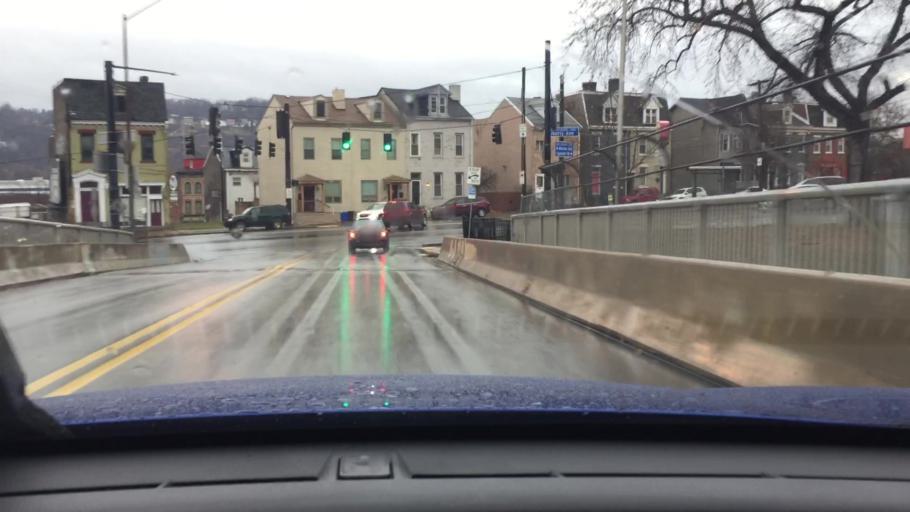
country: US
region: Pennsylvania
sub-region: Allegheny County
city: Bloomfield
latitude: 40.4611
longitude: -79.9669
